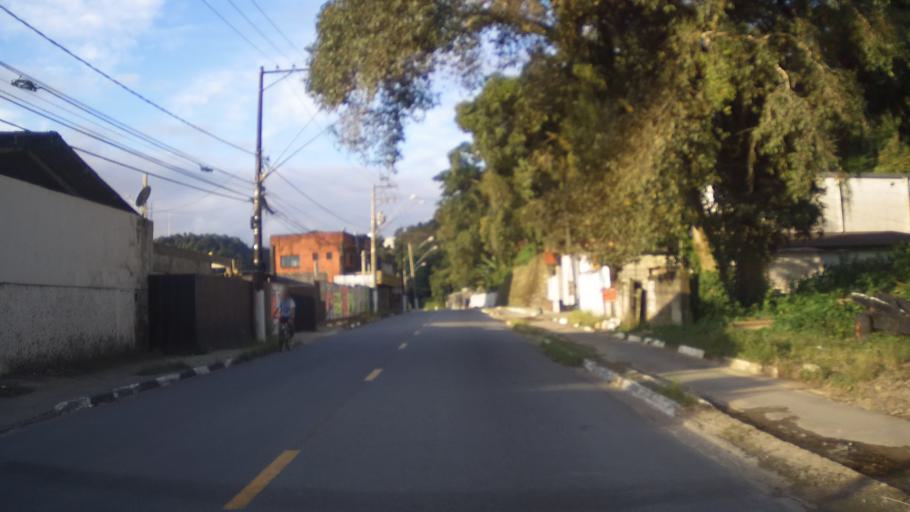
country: BR
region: Sao Paulo
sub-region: Sao Vicente
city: Sao Vicente
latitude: -23.9814
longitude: -46.3915
